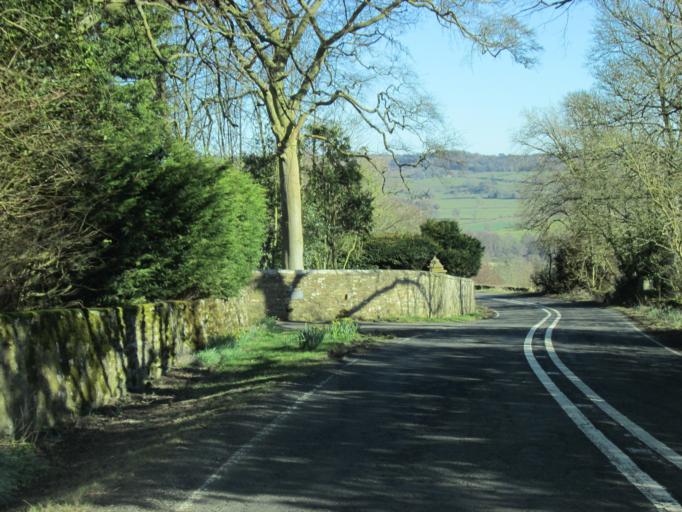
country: GB
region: England
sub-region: Northumberland
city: Wall
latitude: 55.0297
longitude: -2.1574
